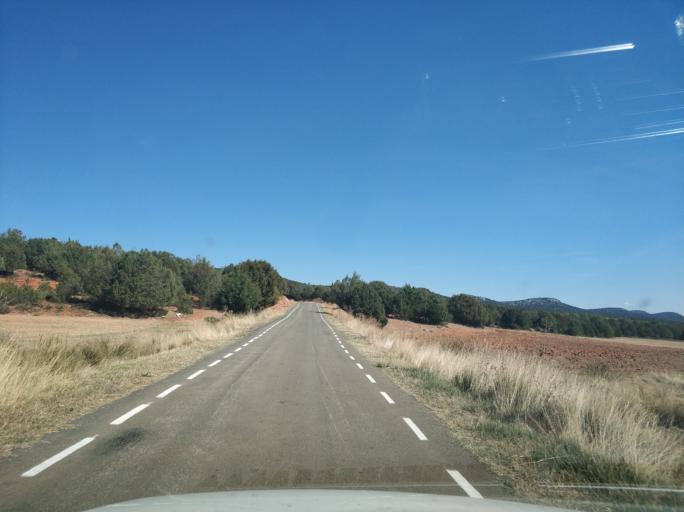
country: ES
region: Castille and Leon
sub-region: Provincia de Soria
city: Santa Maria de las Hoyas
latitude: 41.7501
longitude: -3.1513
